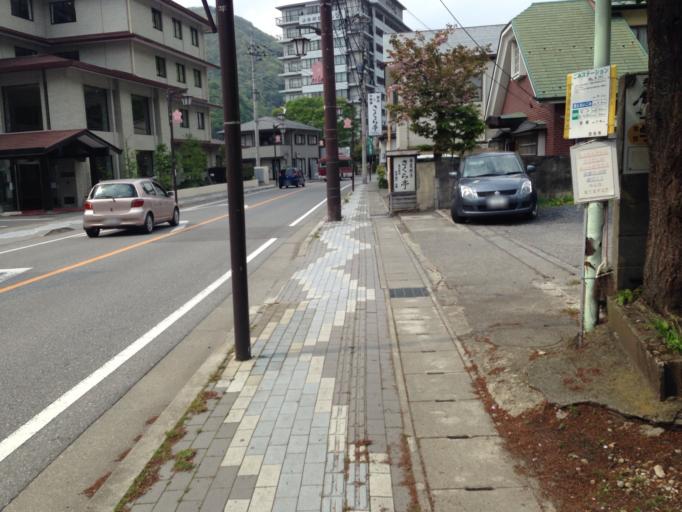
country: JP
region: Tochigi
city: Imaichi
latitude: 36.8280
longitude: 139.7190
